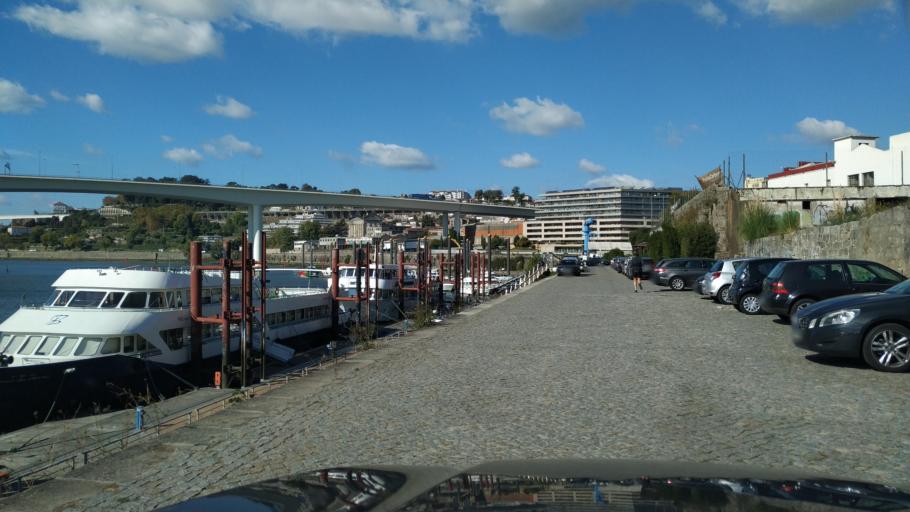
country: PT
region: Porto
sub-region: Gondomar
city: Valbom
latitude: 41.1426
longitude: -8.5760
